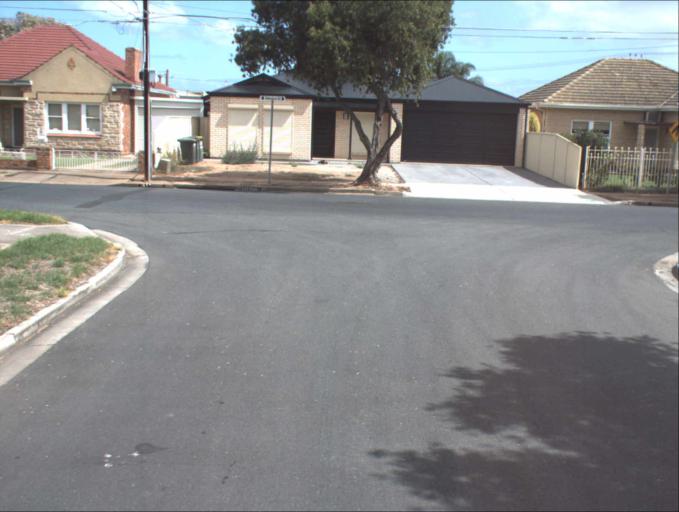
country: AU
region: South Australia
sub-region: Charles Sturt
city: Woodville
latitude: -34.8800
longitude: 138.5611
